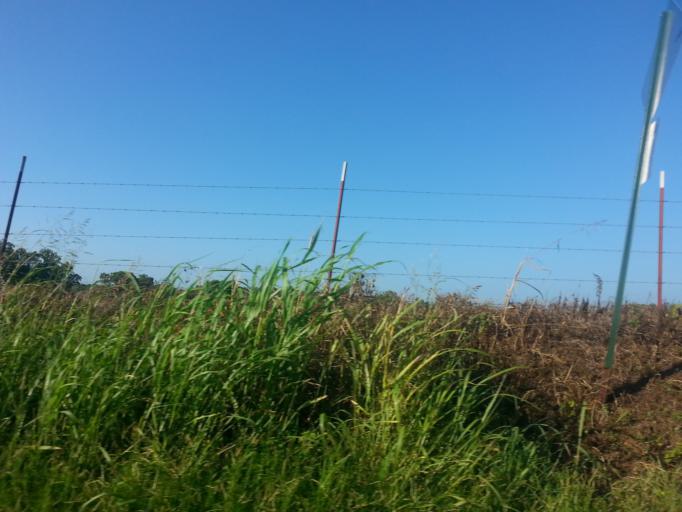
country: US
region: Tennessee
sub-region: Blount County
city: Wildwood
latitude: 35.7516
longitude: -83.8825
